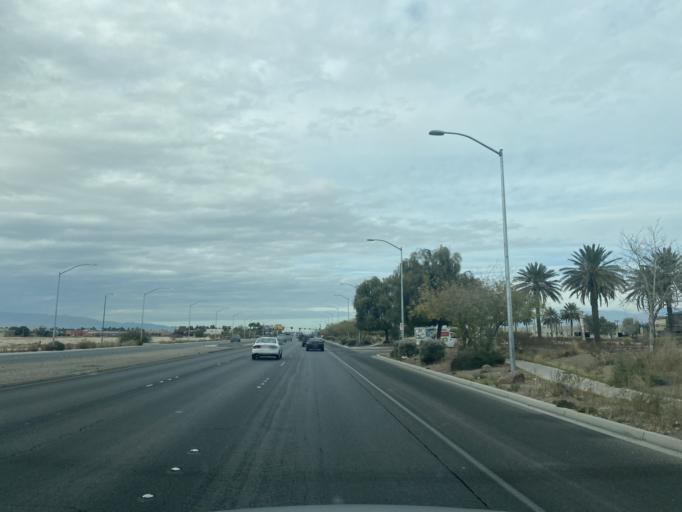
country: US
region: Nevada
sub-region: Clark County
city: Las Vegas
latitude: 36.2043
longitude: -115.2002
